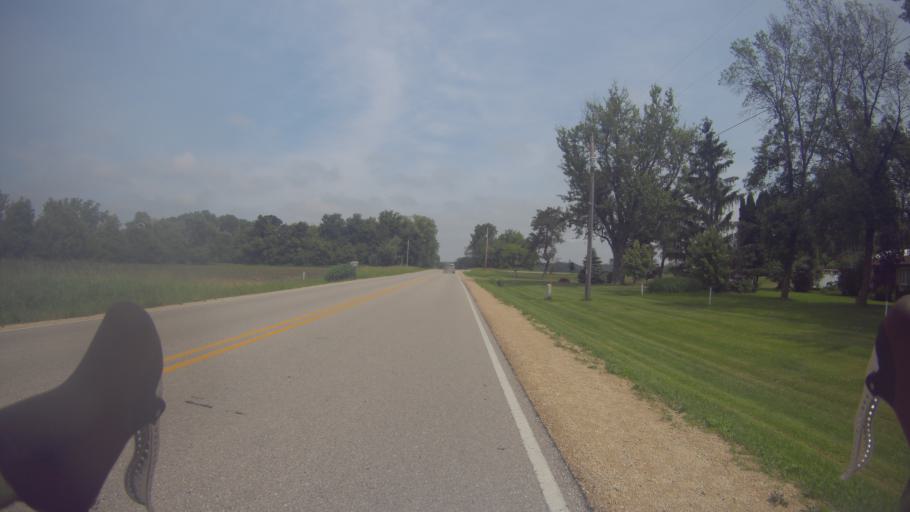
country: US
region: Wisconsin
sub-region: Rock County
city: Edgerton
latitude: 42.8646
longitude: -89.0317
